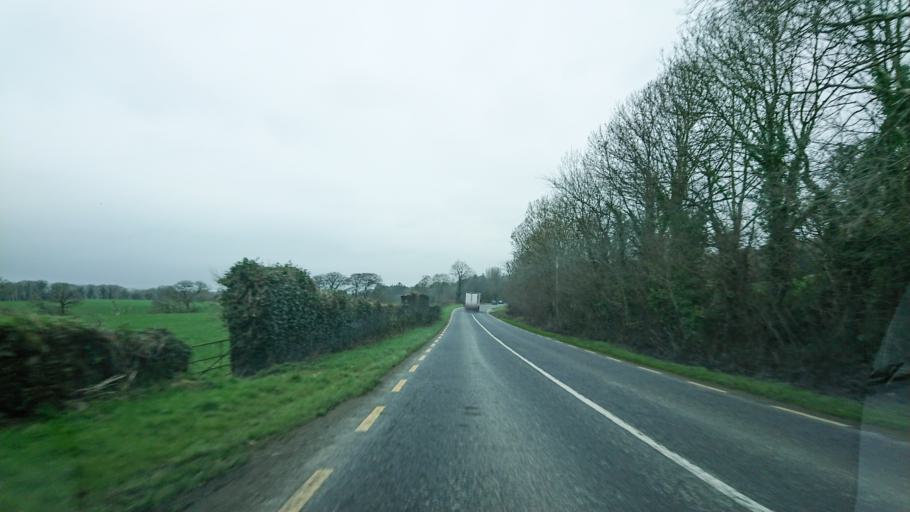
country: IE
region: Munster
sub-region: County Cork
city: Bandon
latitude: 51.7461
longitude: -8.7835
